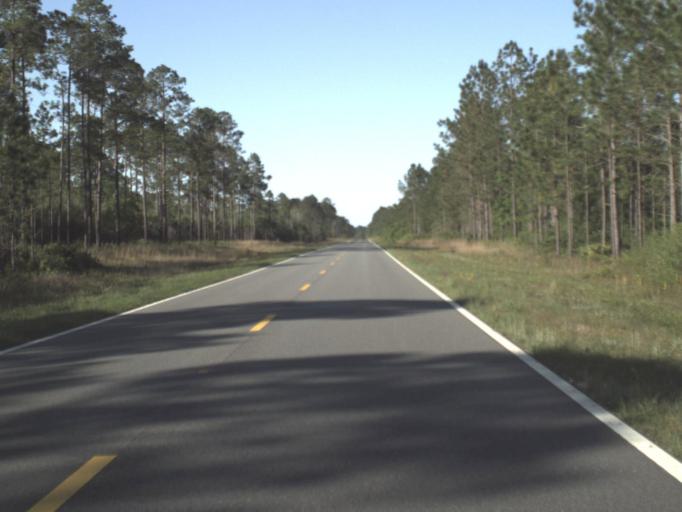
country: US
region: Florida
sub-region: Liberty County
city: Bristol
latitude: 30.2428
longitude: -84.8693
